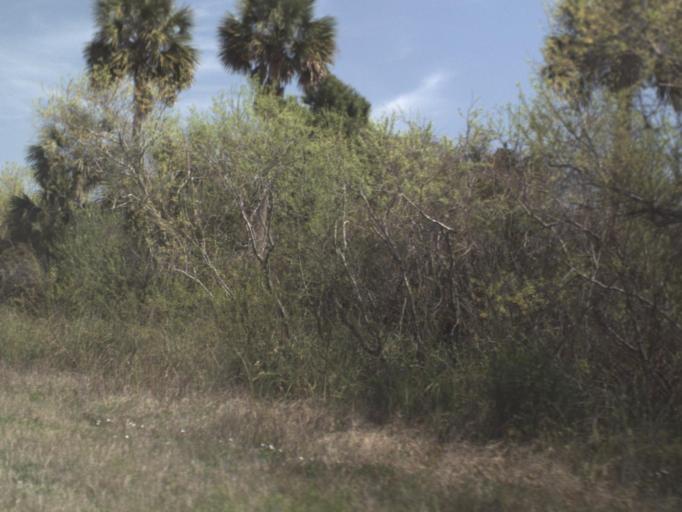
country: US
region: Florida
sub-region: Gulf County
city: Port Saint Joe
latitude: 29.6748
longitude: -85.3464
